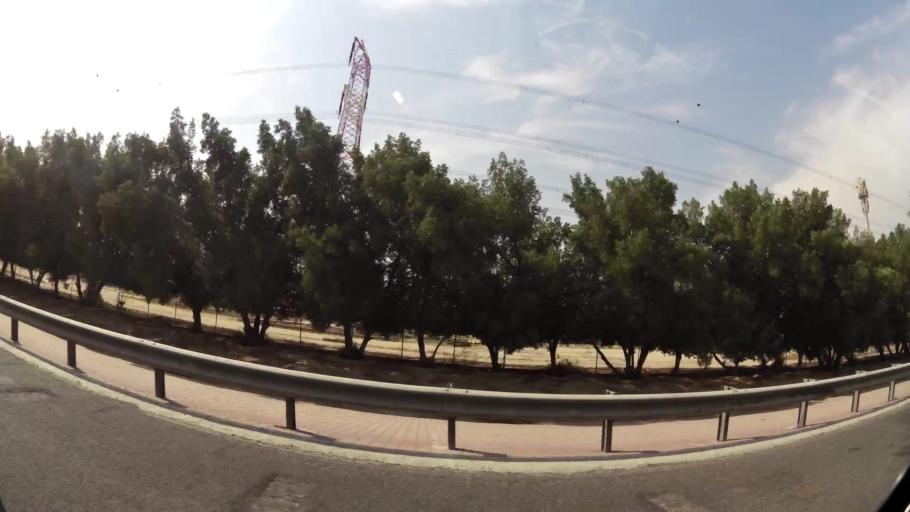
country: KW
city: Bayan
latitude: 29.2842
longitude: 48.0325
